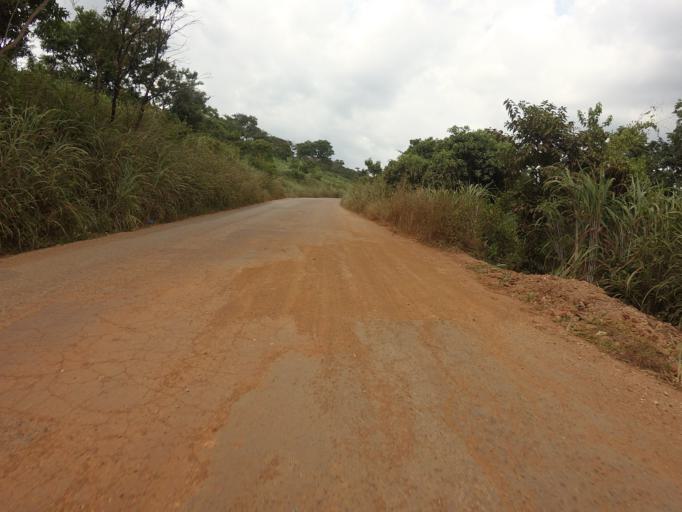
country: GH
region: Volta
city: Ho
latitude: 6.6756
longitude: 0.3520
